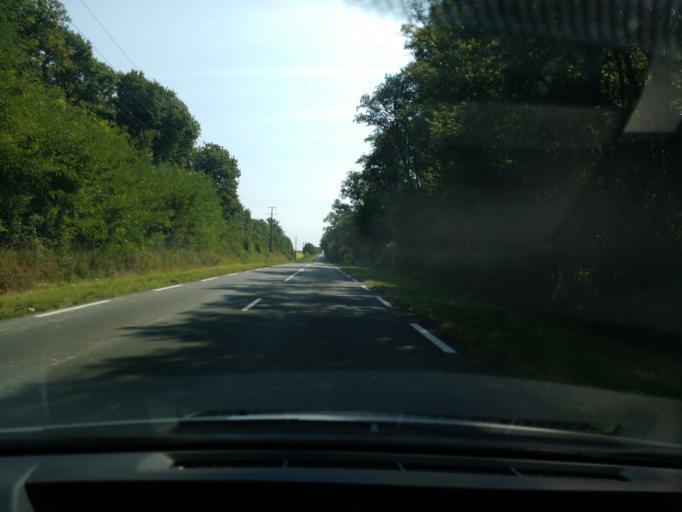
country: FR
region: Pays de la Loire
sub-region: Departement de Maine-et-Loire
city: Bauge-en-Anjou
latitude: 47.5324
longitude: -0.0586
